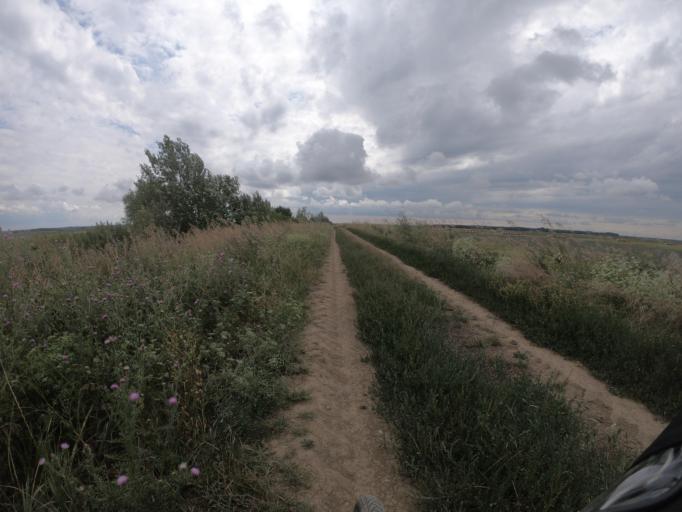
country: HU
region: Jasz-Nagykun-Szolnok
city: Tiszafured
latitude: 47.7212
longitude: 20.7893
